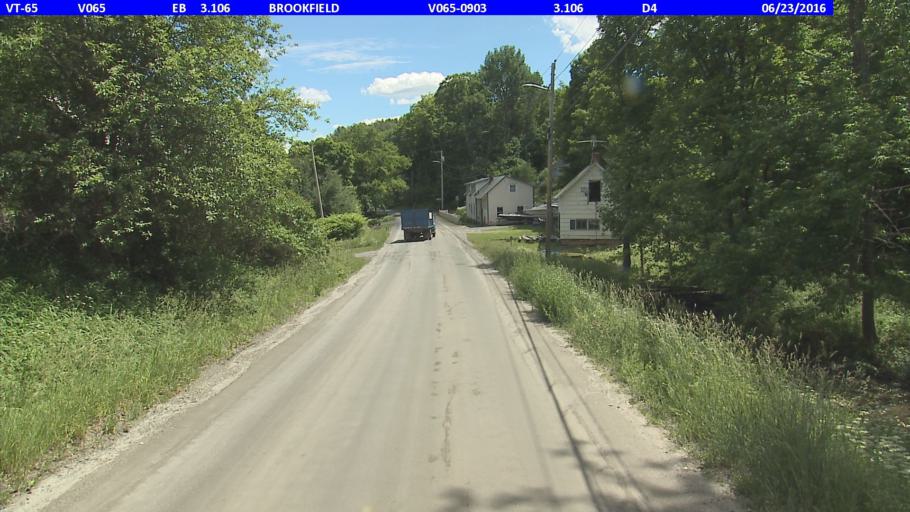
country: US
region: Vermont
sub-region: Orange County
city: Williamstown
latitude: 44.0413
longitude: -72.6032
